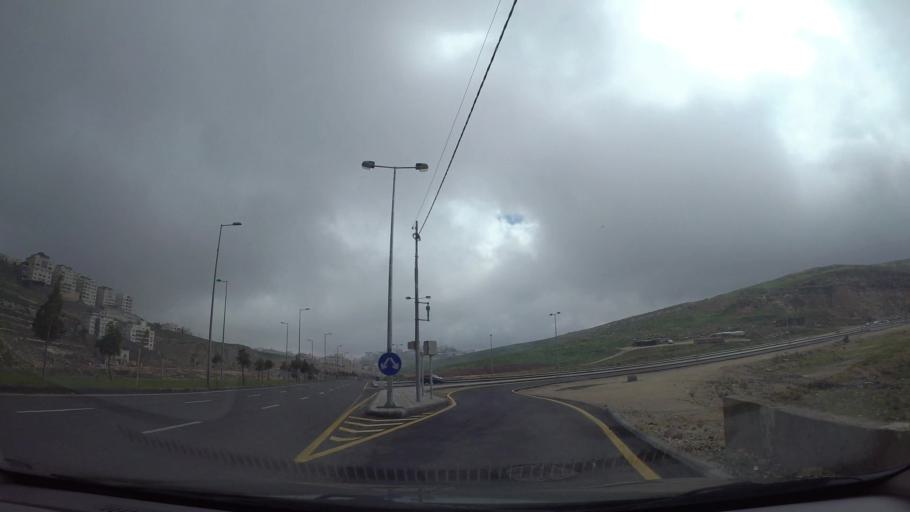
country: JO
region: Amman
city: Al Bunayyat ash Shamaliyah
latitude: 31.9355
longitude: 35.8730
